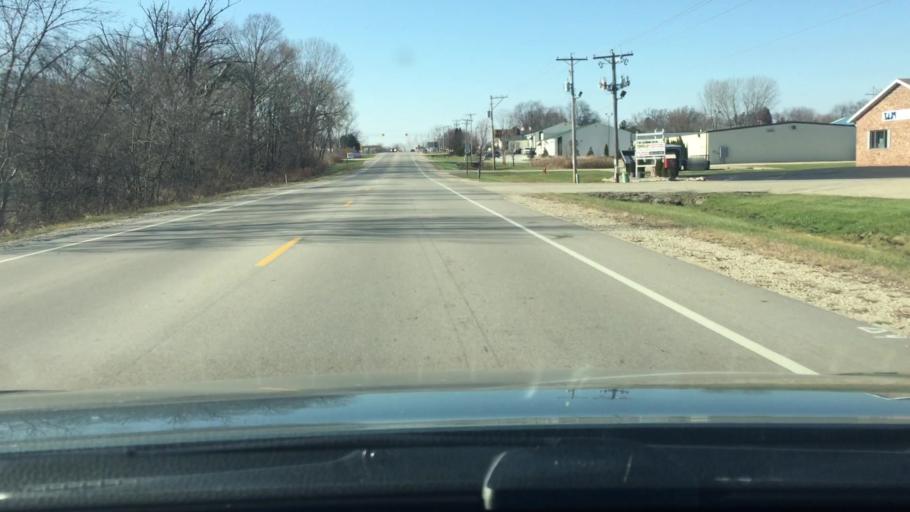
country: US
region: Wisconsin
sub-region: Jefferson County
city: Cambridge
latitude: 43.0088
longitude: -89.0165
